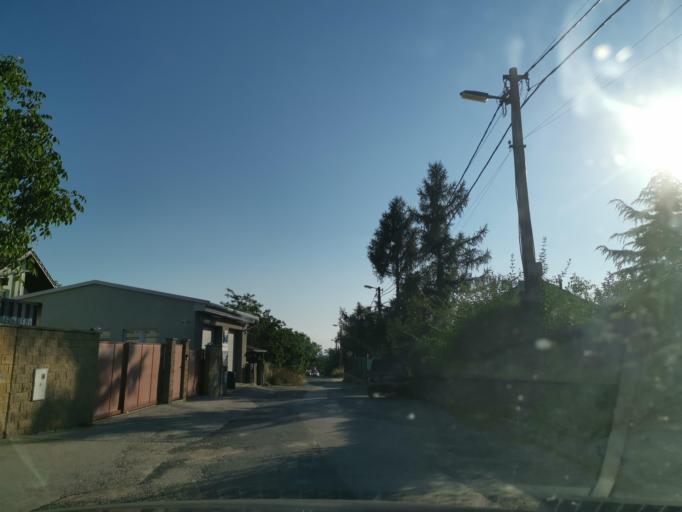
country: SK
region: Bratislavsky
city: Stupava
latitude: 48.2808
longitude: 17.0434
